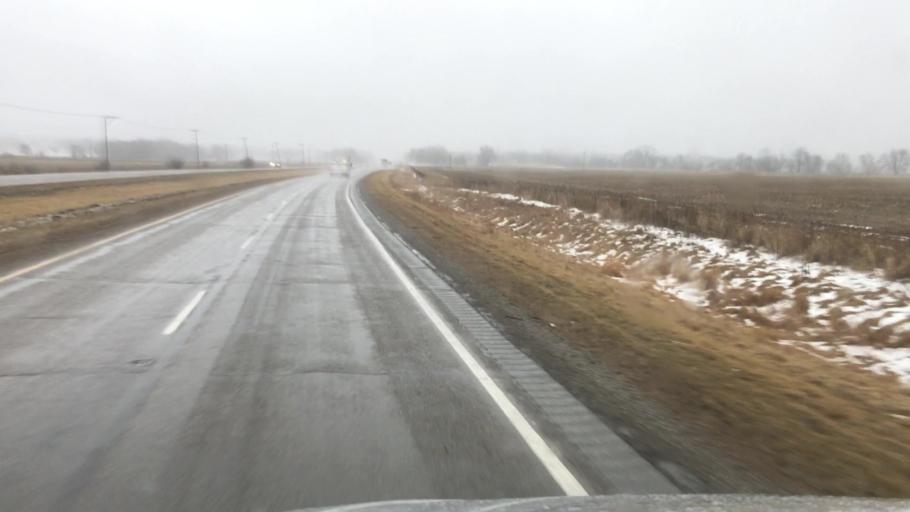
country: US
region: Indiana
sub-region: Newton County
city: Roselawn
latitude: 41.1199
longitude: -87.4490
